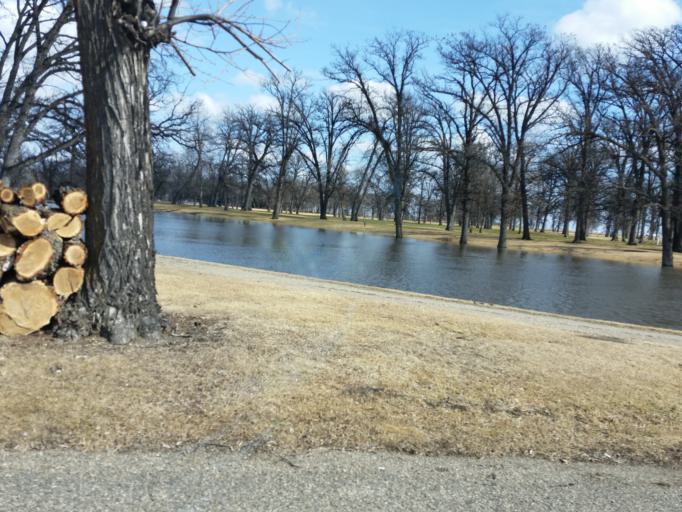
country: US
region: North Dakota
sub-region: Walsh County
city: Grafton
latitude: 48.4209
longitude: -97.3916
